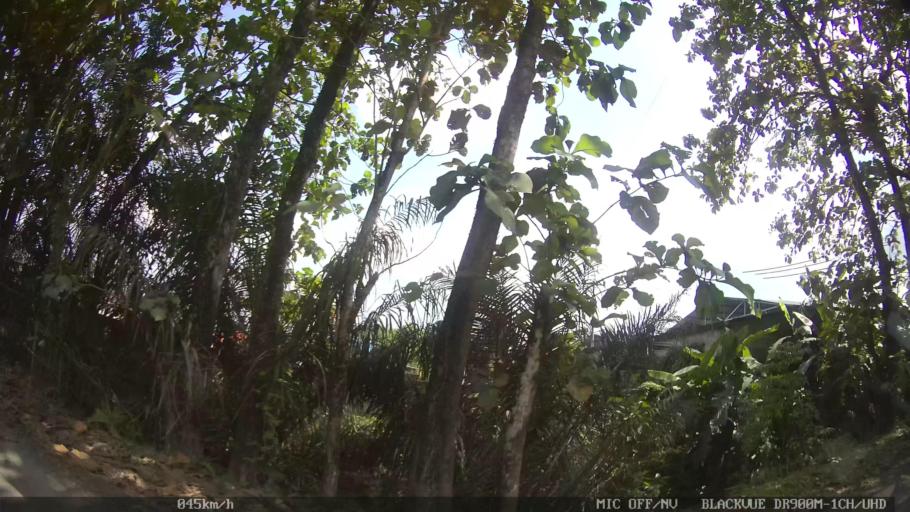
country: ID
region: North Sumatra
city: Binjai
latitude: 3.6349
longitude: 98.5312
